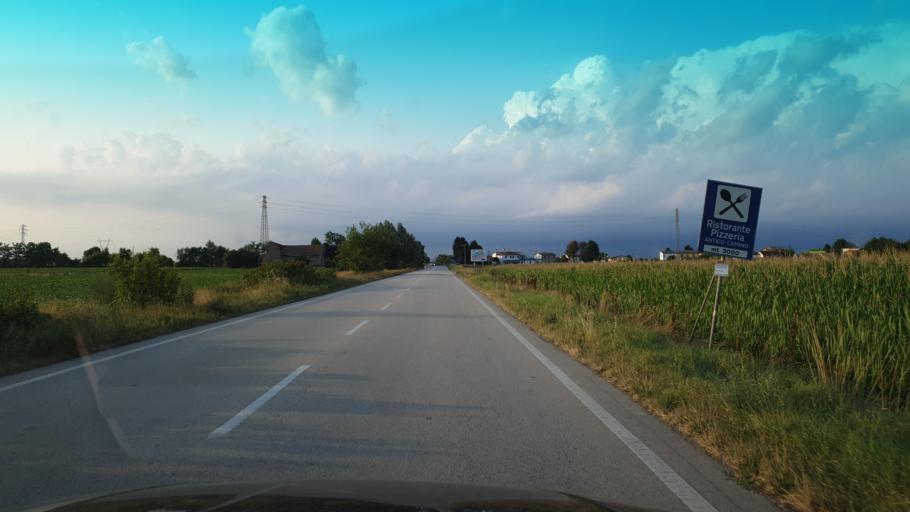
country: IT
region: Veneto
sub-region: Provincia di Rovigo
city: San Bellino
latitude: 45.0427
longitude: 11.5809
